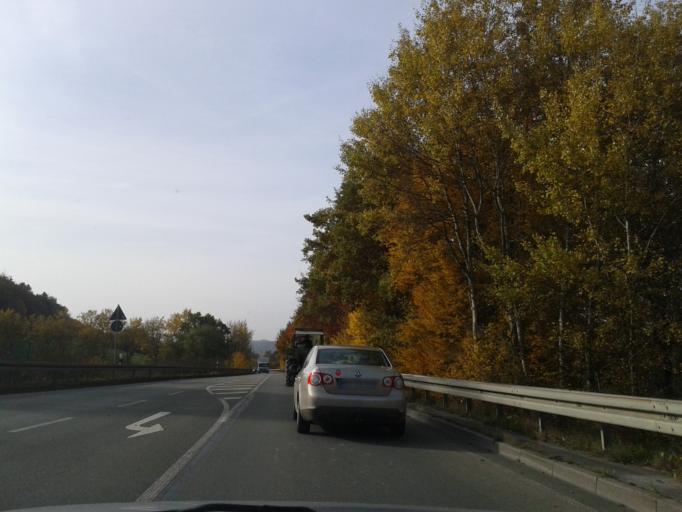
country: DE
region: North Rhine-Westphalia
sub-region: Regierungsbezirk Arnsberg
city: Ruthen
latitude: 51.4682
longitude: 8.4424
